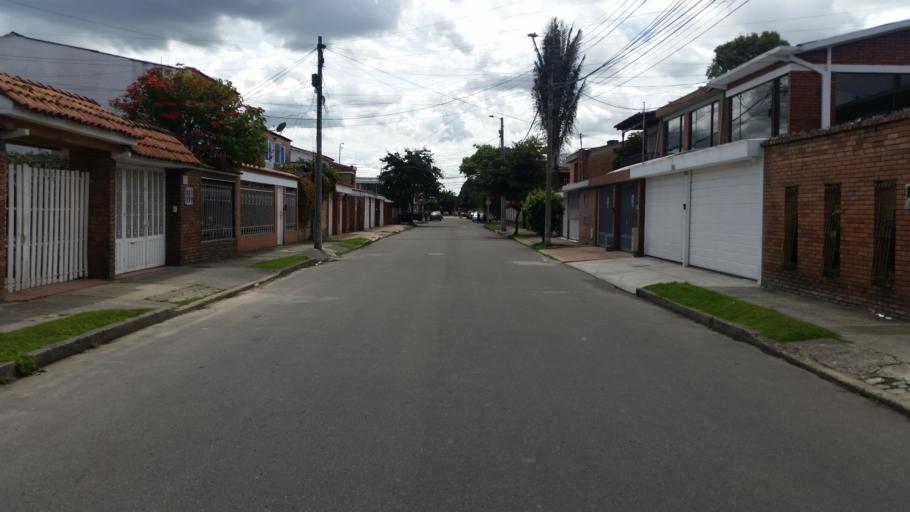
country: CO
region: Bogota D.C.
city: Bogota
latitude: 4.6481
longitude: -74.0927
